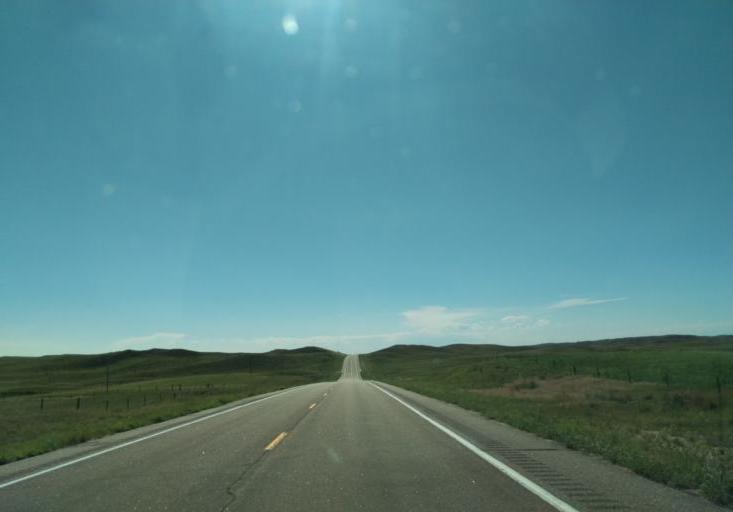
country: US
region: South Dakota
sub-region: Bennett County
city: Martin
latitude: 42.9218
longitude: -101.5297
